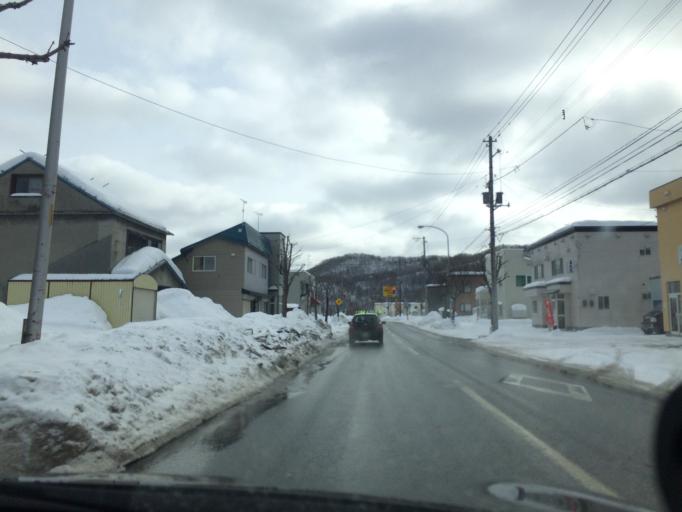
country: JP
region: Hokkaido
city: Iwamizawa
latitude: 43.0236
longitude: 141.9741
